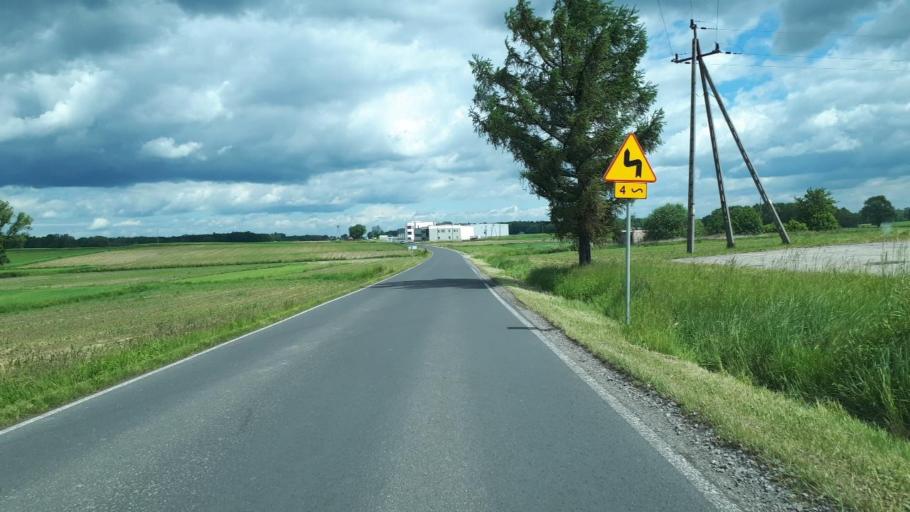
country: PL
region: Silesian Voivodeship
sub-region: Powiat bielski
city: Wilamowice
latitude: 49.9252
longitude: 19.1498
